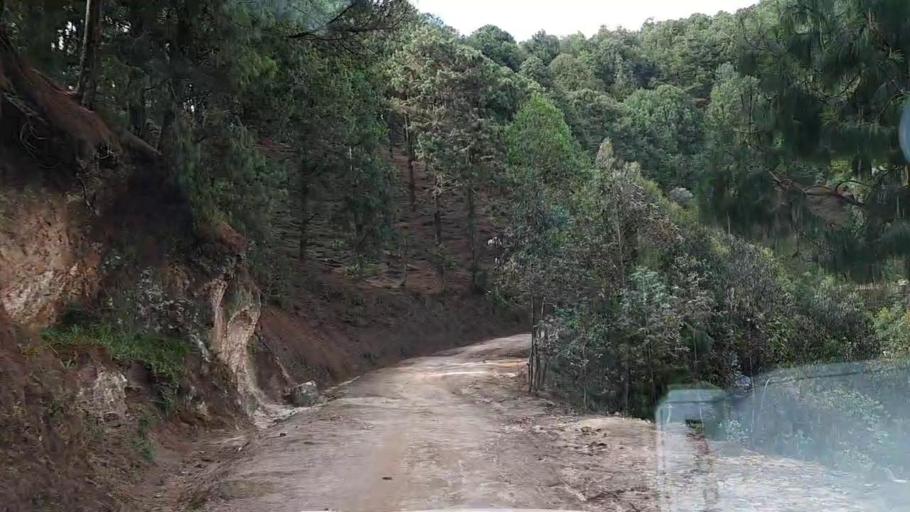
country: RW
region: Southern Province
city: Nzega
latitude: -2.4102
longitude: 29.4556
